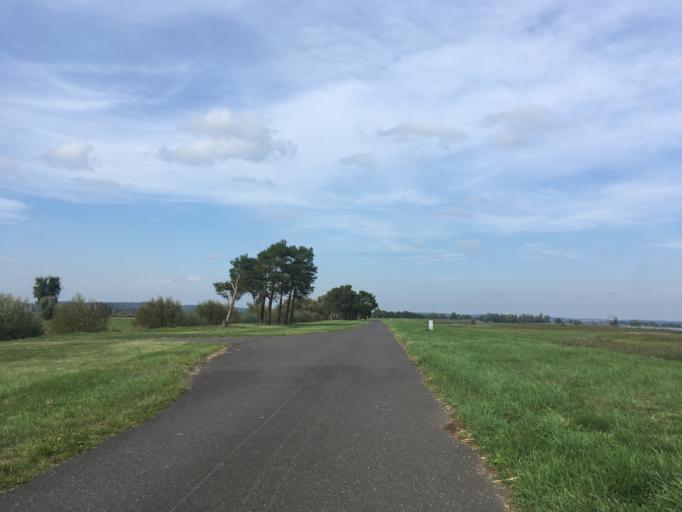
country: DE
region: Brandenburg
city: Schoneberg
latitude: 52.9298
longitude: 14.1390
